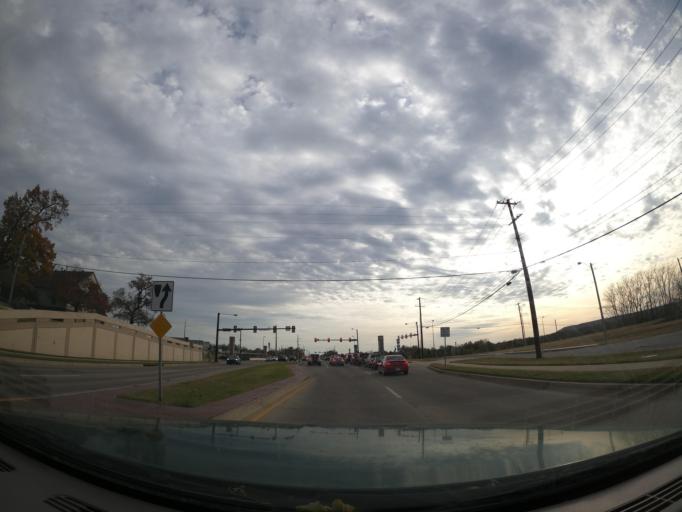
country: US
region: Oklahoma
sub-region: Tulsa County
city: Jenks
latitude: 36.0917
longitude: -95.9581
